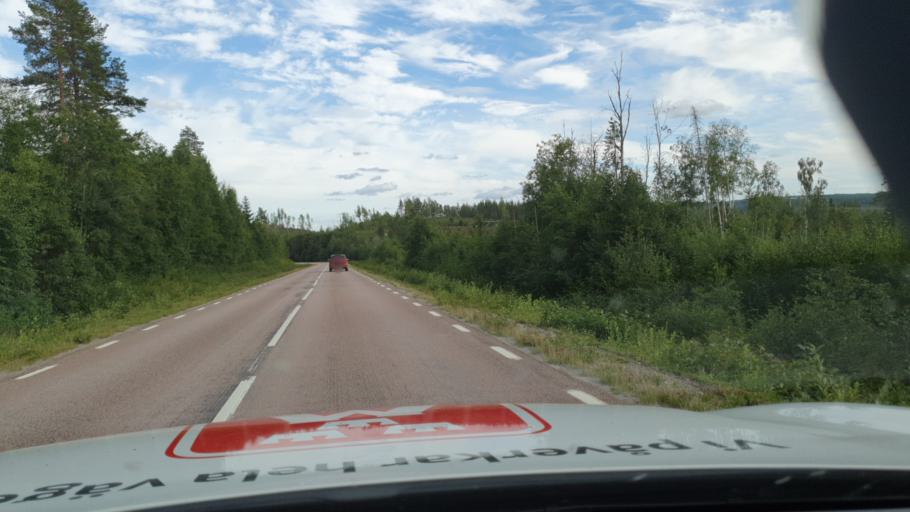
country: SE
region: Vaesternorrland
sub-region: Solleftea Kommun
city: As
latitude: 63.6108
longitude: 16.1081
